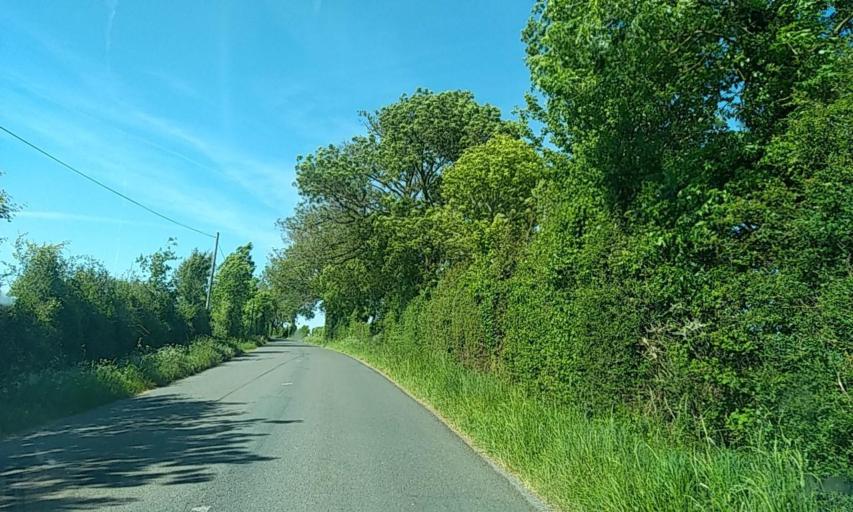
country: FR
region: Poitou-Charentes
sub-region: Departement des Deux-Sevres
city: Boisme
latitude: 46.7905
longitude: -0.4517
